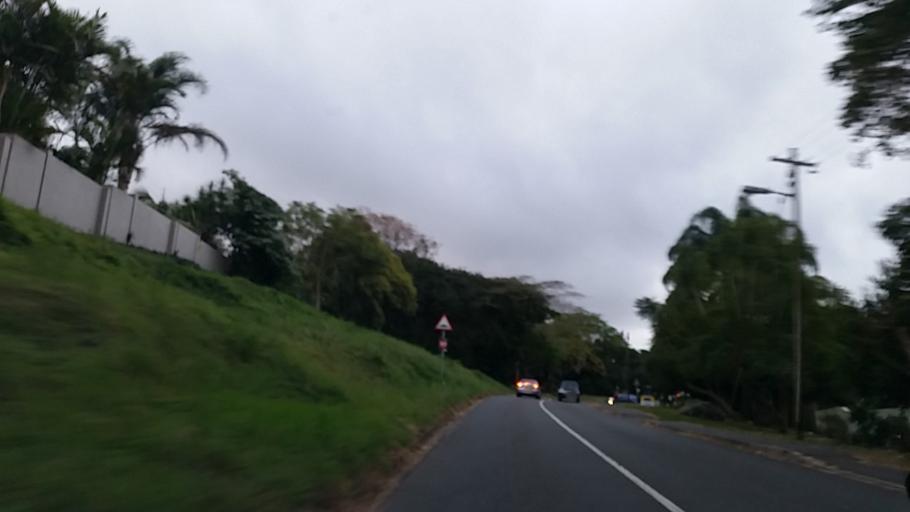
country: ZA
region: KwaZulu-Natal
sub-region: eThekwini Metropolitan Municipality
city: Berea
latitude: -29.8438
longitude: 30.9054
